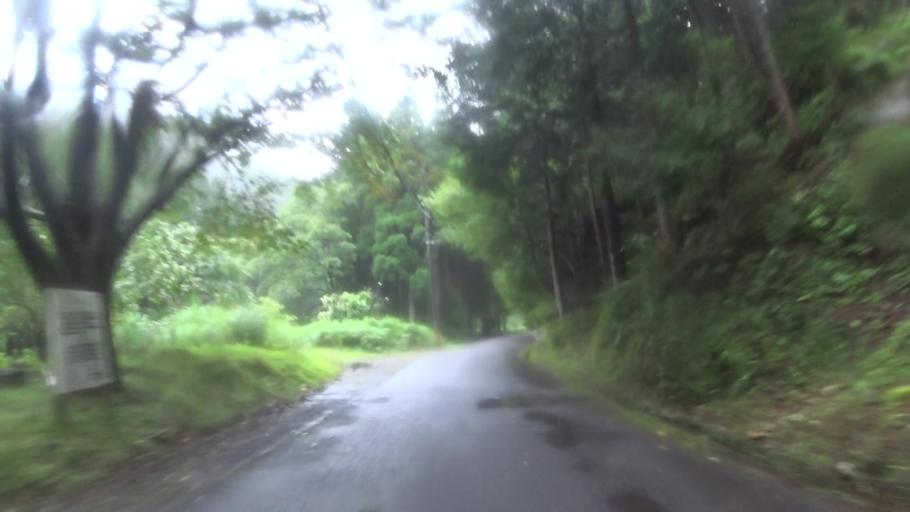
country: JP
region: Shiga Prefecture
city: Kitahama
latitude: 35.2749
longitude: 135.8495
